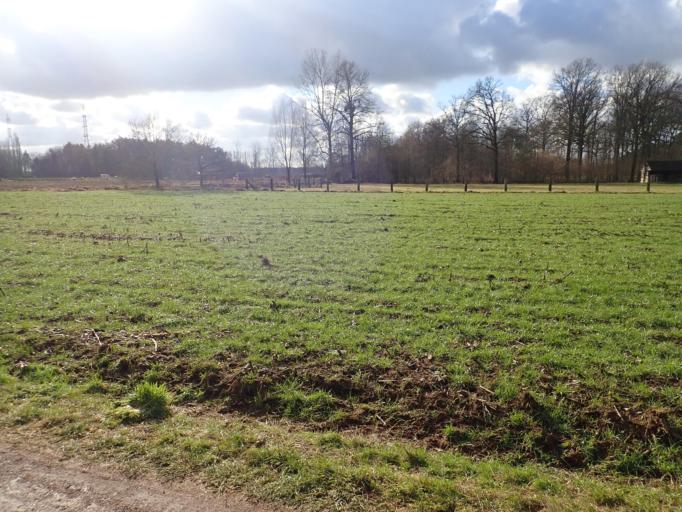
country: BE
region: Flanders
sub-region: Provincie Antwerpen
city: Zandhoven
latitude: 51.2319
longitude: 4.6917
